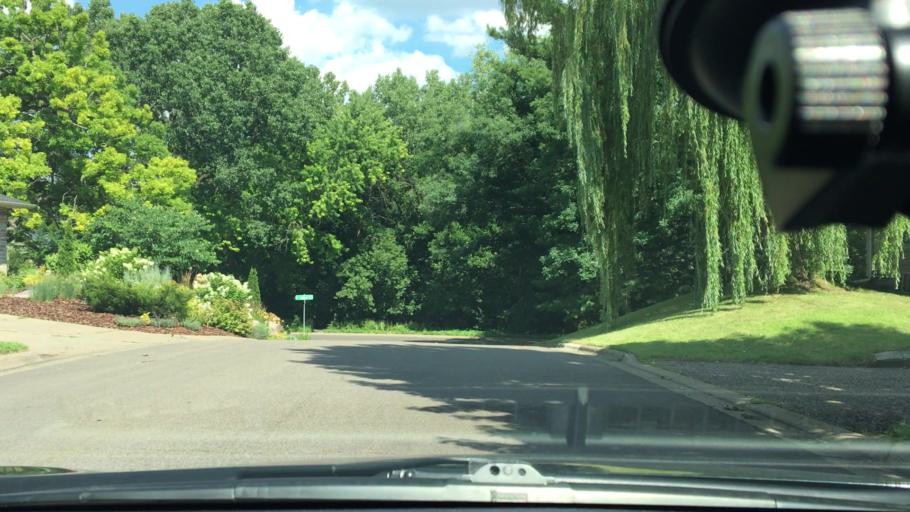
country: US
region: Minnesota
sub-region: Hennepin County
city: Golden Valley
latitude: 44.9944
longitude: -93.3878
